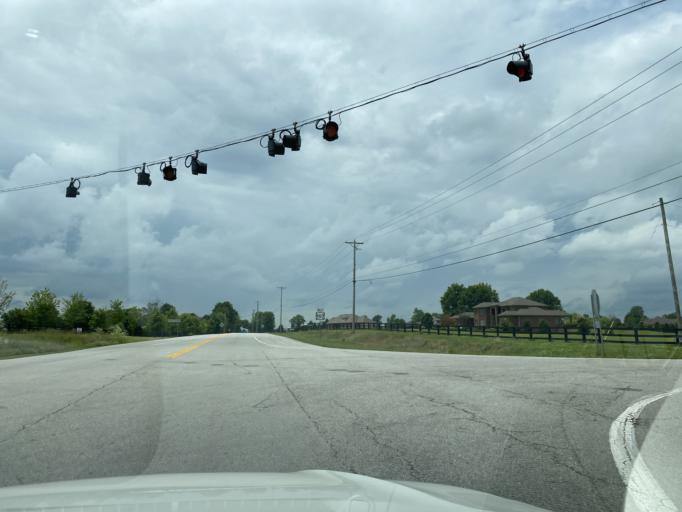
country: US
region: Kentucky
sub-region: Scott County
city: Georgetown
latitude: 38.2194
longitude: -84.4810
